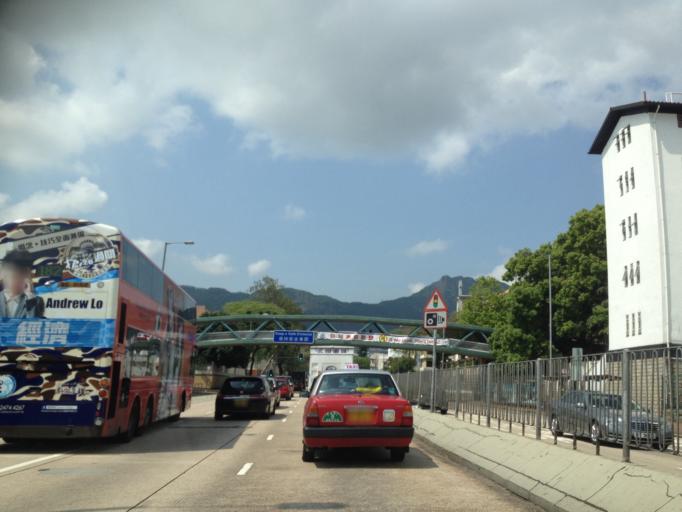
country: HK
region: Kowloon City
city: Kowloon
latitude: 22.3293
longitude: 114.1785
